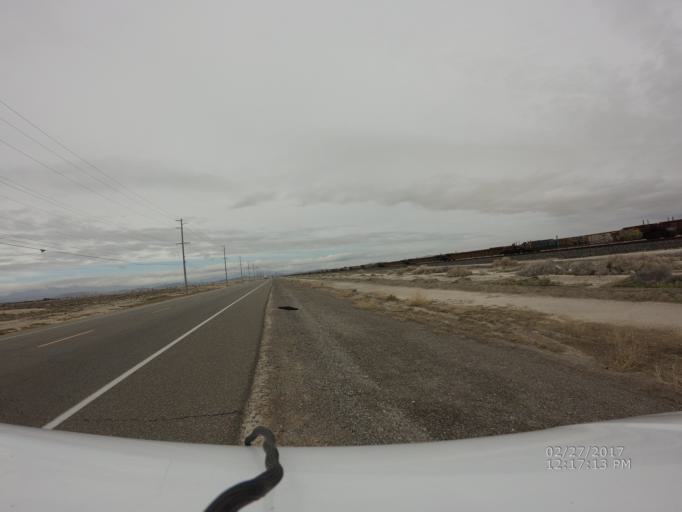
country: US
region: California
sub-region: Los Angeles County
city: Lancaster
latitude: 34.7694
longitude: -118.1479
